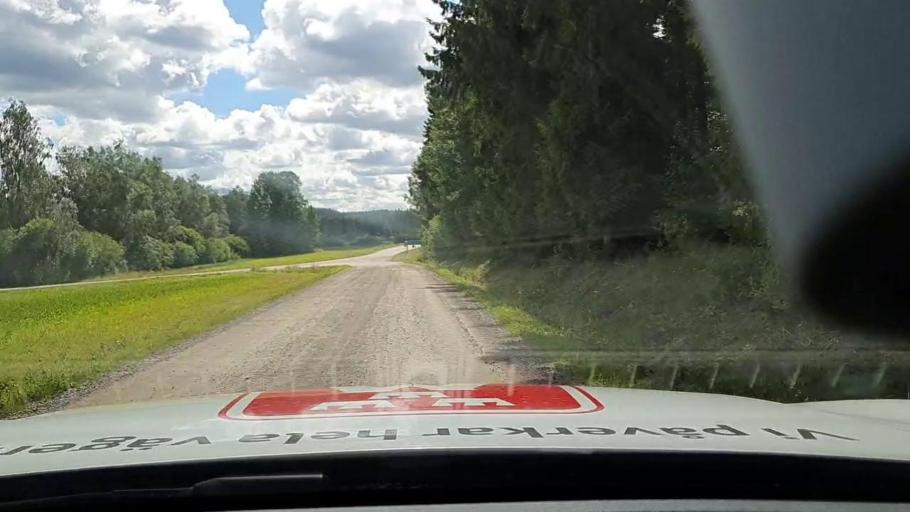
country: SE
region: Vaestra Goetaland
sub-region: Karlsborgs Kommun
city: Molltorp
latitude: 58.6117
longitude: 14.3372
